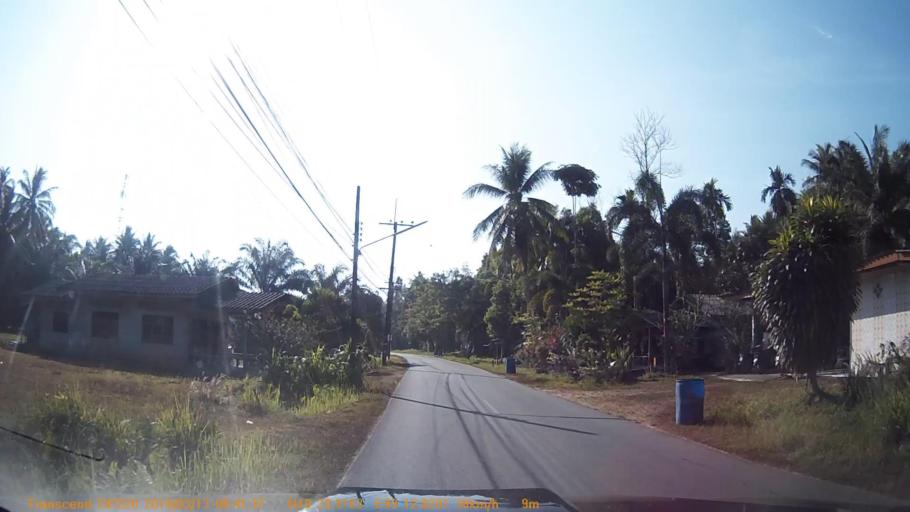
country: TH
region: Chumphon
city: Chumphon
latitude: 10.4988
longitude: 99.2136
